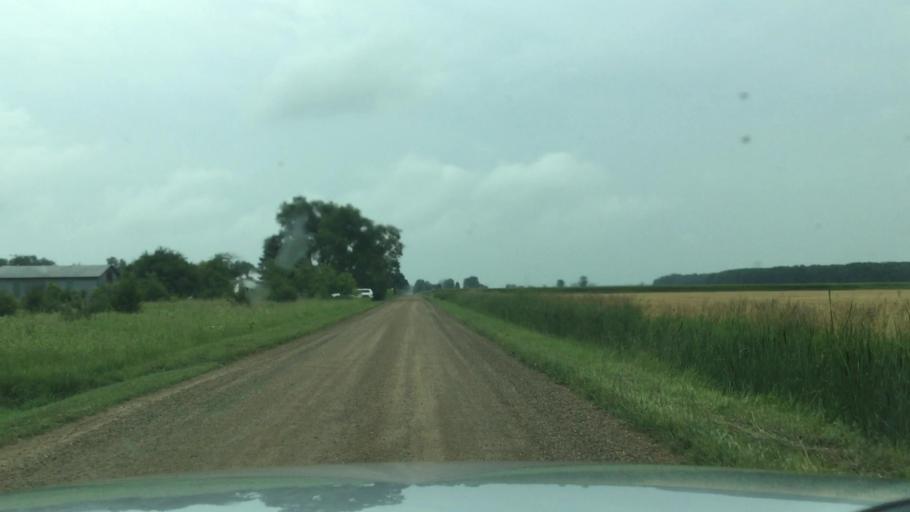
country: US
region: Michigan
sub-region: Shiawassee County
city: New Haven
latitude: 43.1155
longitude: -84.2303
